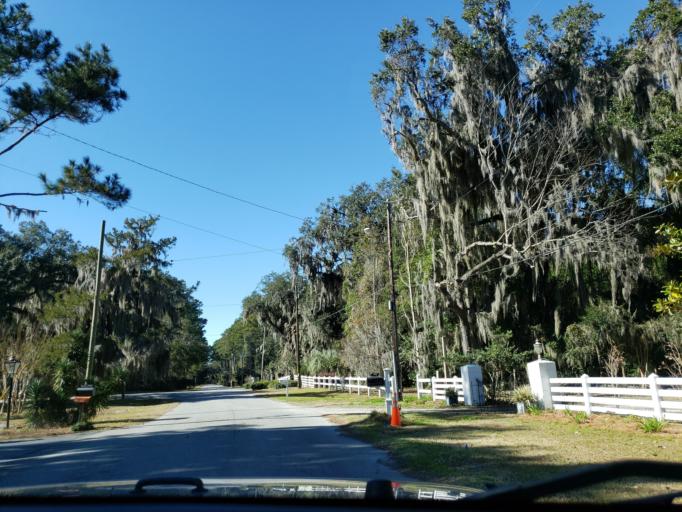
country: US
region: Georgia
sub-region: Chatham County
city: Wilmington Island
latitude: 32.0401
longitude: -80.9718
